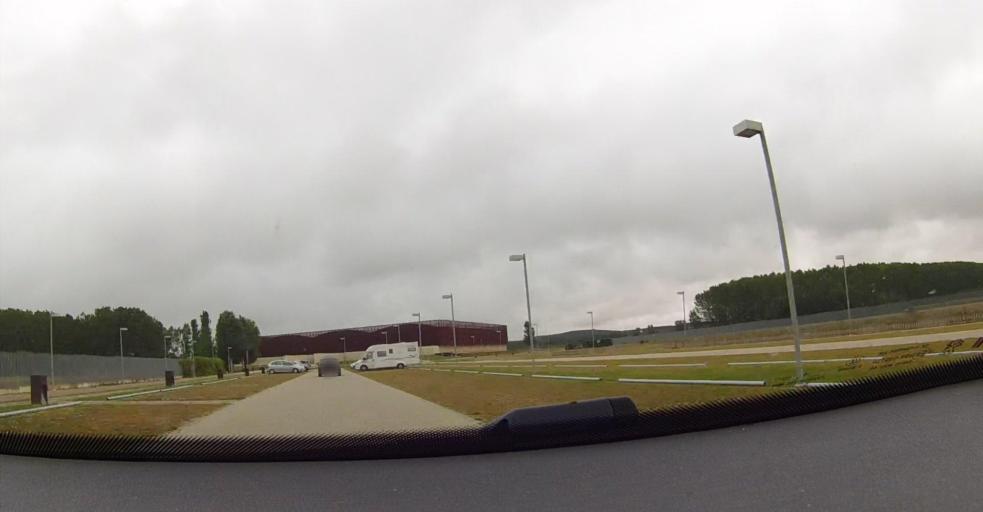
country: ES
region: Castille and Leon
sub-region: Provincia de Palencia
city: Pedrosa de la Vega
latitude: 42.4799
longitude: -4.7361
